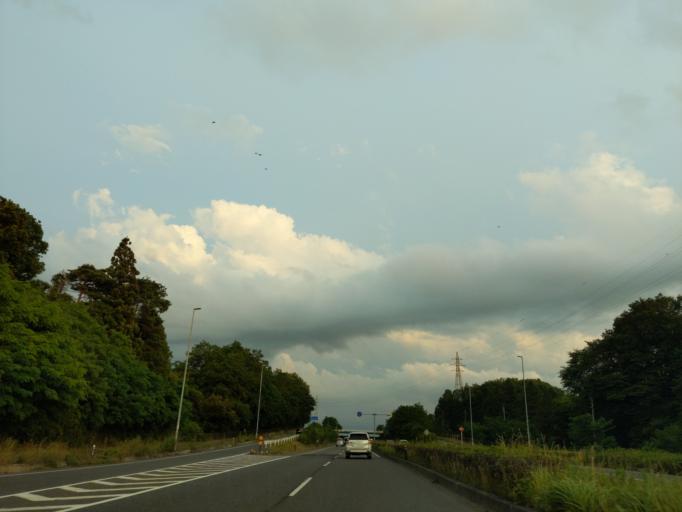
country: JP
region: Fukushima
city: Koriyama
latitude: 37.3600
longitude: 140.3511
